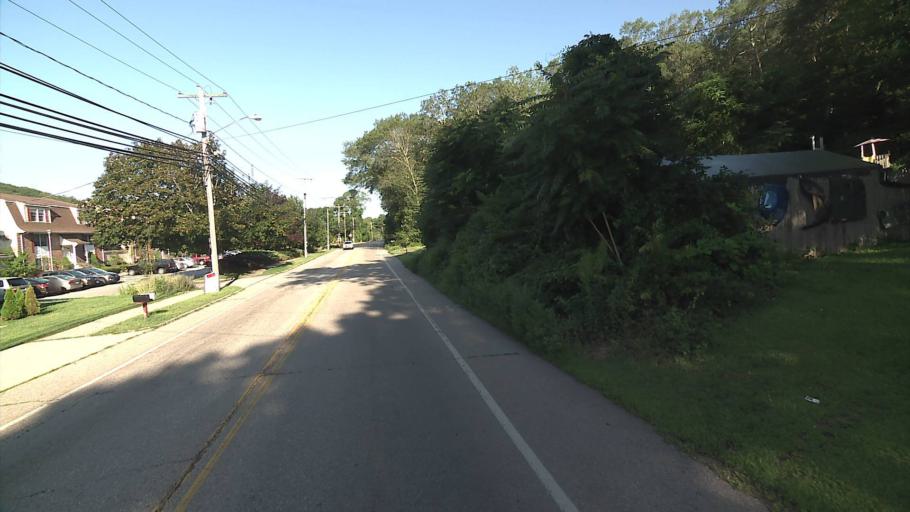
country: US
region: Connecticut
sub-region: New London County
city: Central Waterford
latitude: 41.3496
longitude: -72.1498
